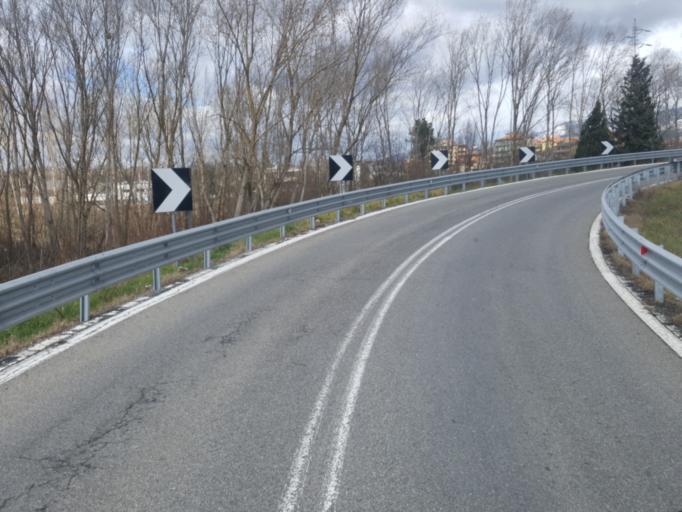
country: IT
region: Calabria
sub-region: Provincia di Cosenza
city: Santo Stefano di Rogliano
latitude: 39.1990
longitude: 16.3108
